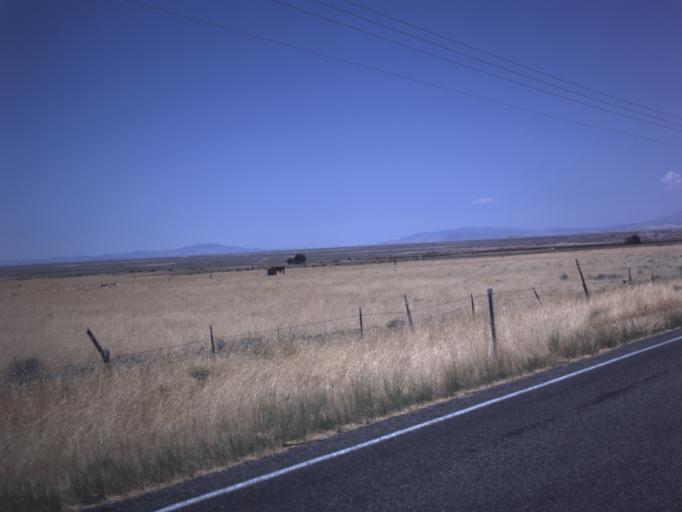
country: US
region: Utah
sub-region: Millard County
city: Delta
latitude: 39.3915
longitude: -112.3355
